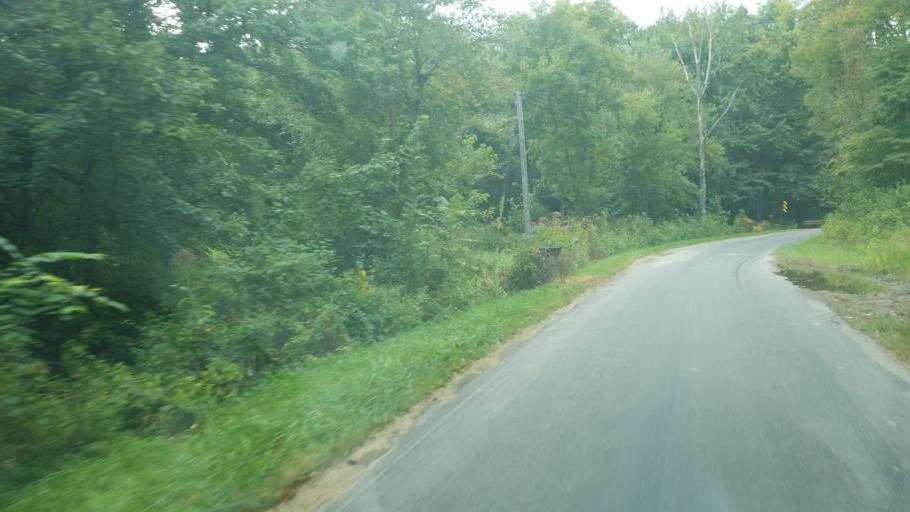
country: US
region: Ohio
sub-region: Jackson County
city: Oak Hill
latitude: 38.9326
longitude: -82.6192
